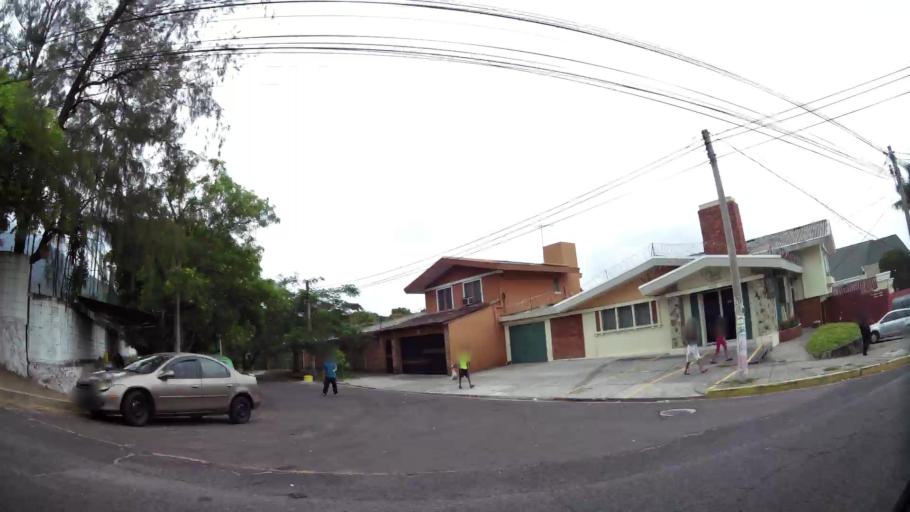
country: SV
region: San Salvador
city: Mejicanos
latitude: 13.7107
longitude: -89.2458
